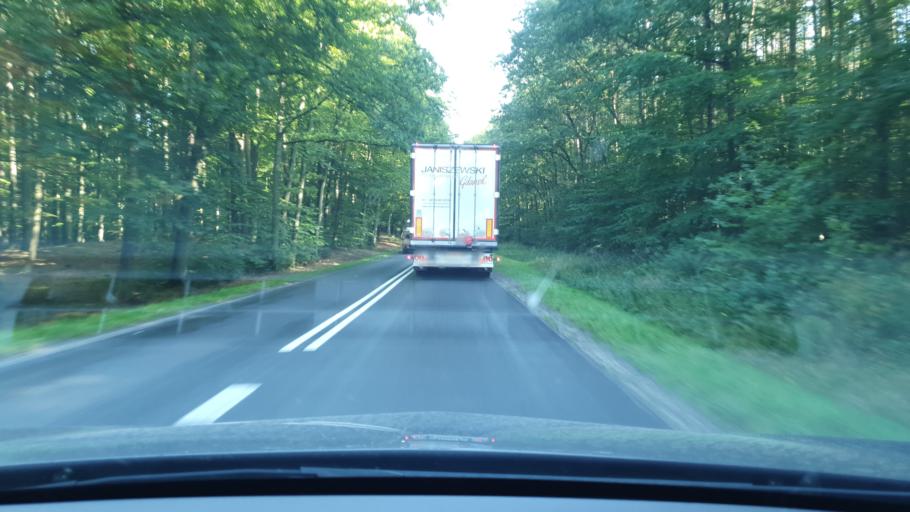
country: PL
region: West Pomeranian Voivodeship
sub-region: Powiat kamienski
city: Golczewo
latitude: 53.8102
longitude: 15.0042
